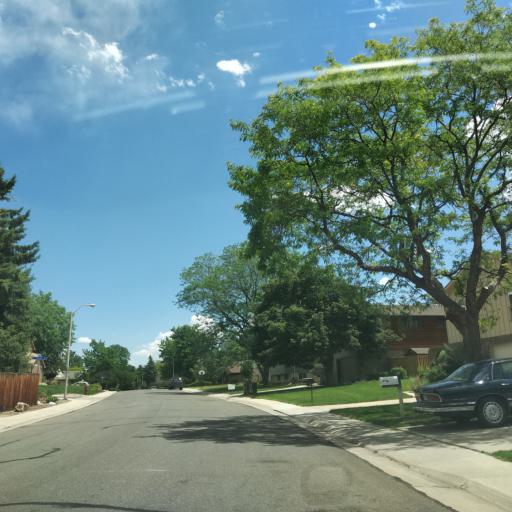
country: US
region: Colorado
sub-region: Jefferson County
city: Lakewood
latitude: 39.6861
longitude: -105.1079
